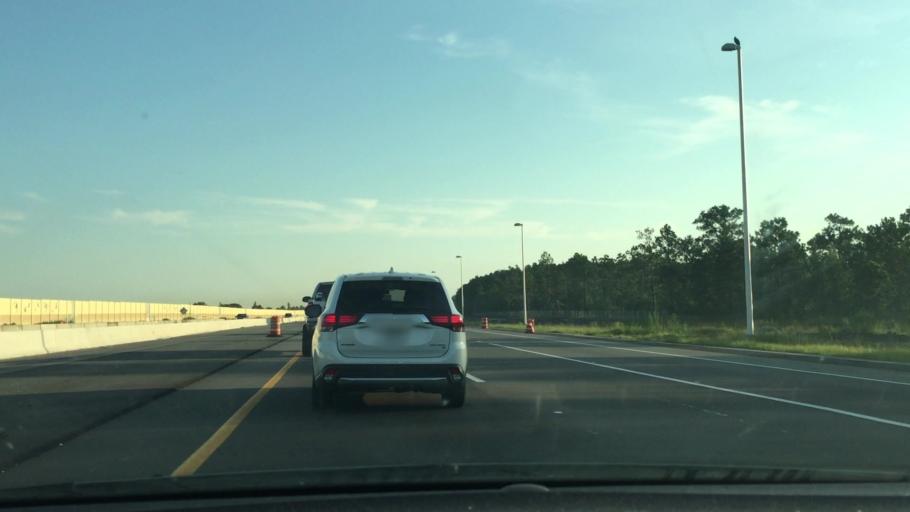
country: US
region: Florida
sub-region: Orange County
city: Southchase
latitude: 28.3797
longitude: -81.3905
